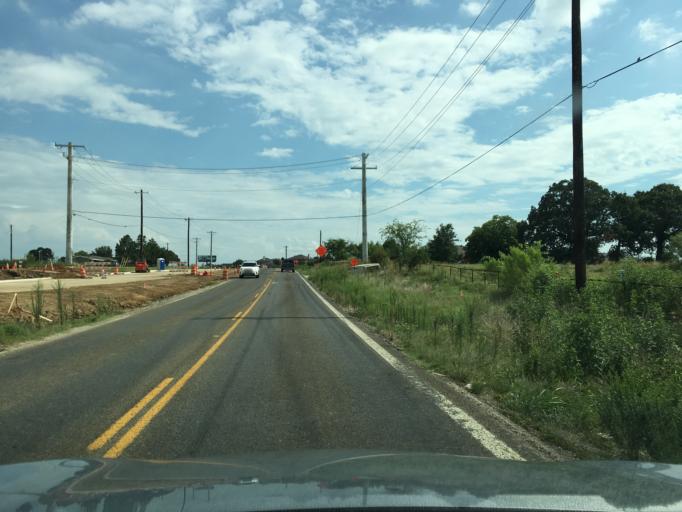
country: US
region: Texas
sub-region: Denton County
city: Cross Roads
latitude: 33.2182
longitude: -96.9767
